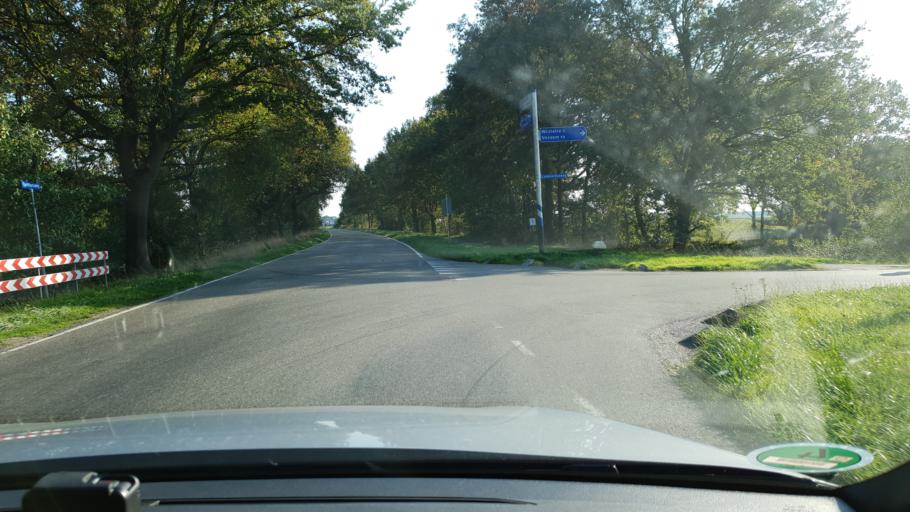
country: NL
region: North Brabant
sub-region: Gemeente Eindhoven
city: Meerhoven
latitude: 51.4685
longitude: 5.3917
